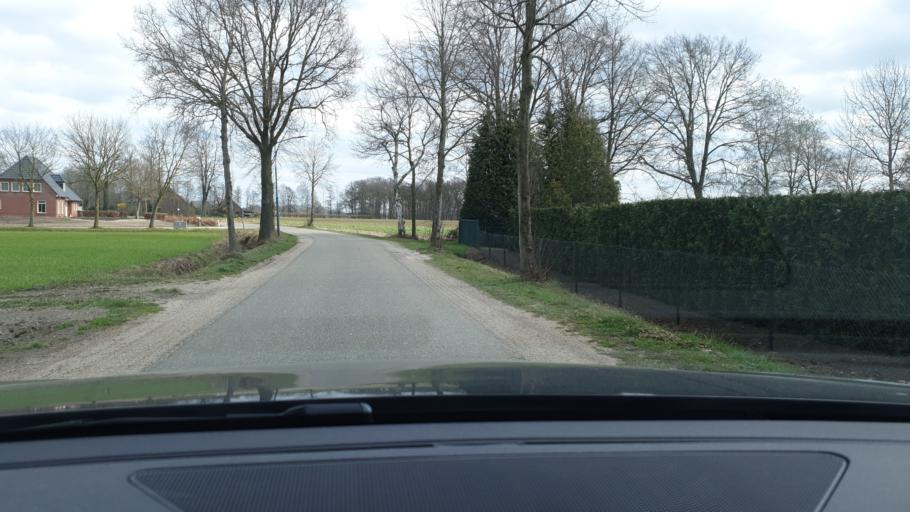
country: NL
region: North Brabant
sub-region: Gemeente Eersel
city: Eersel
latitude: 51.3893
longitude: 5.2732
